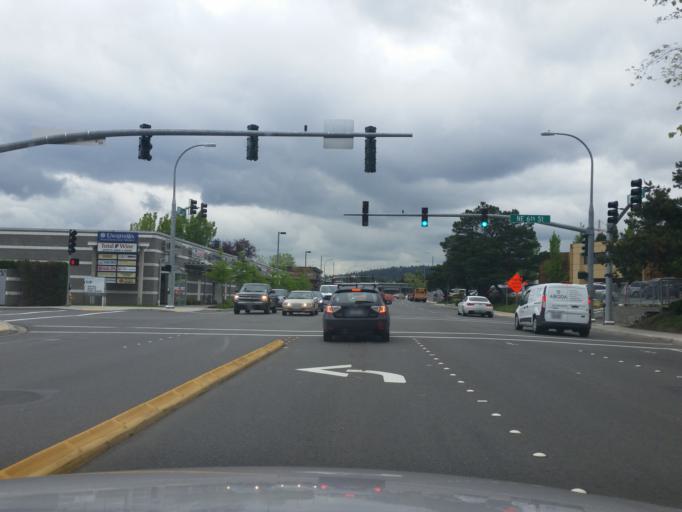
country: US
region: Washington
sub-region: King County
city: Bellevue
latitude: 47.6152
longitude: -122.1803
